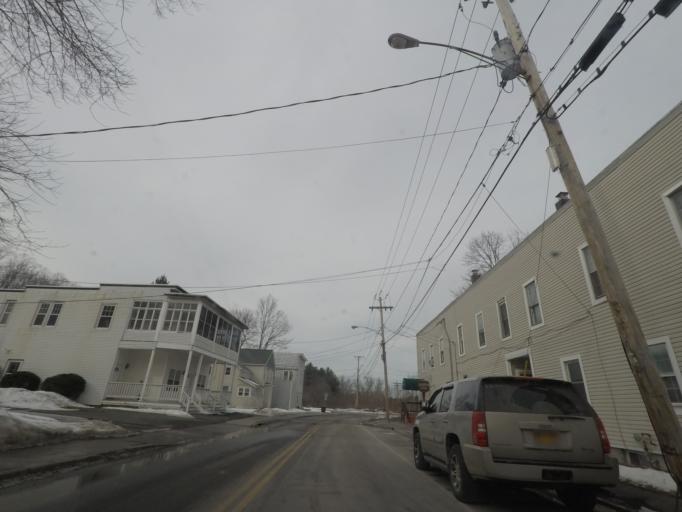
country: US
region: New York
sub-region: Albany County
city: Voorheesville
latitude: 42.6546
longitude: -73.9293
